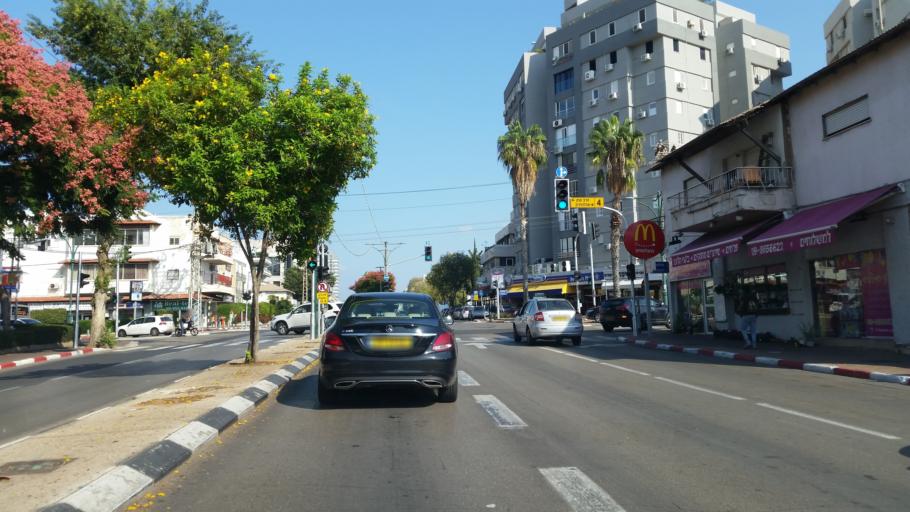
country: IL
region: Tel Aviv
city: Ramat HaSharon
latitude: 32.1605
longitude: 34.8425
